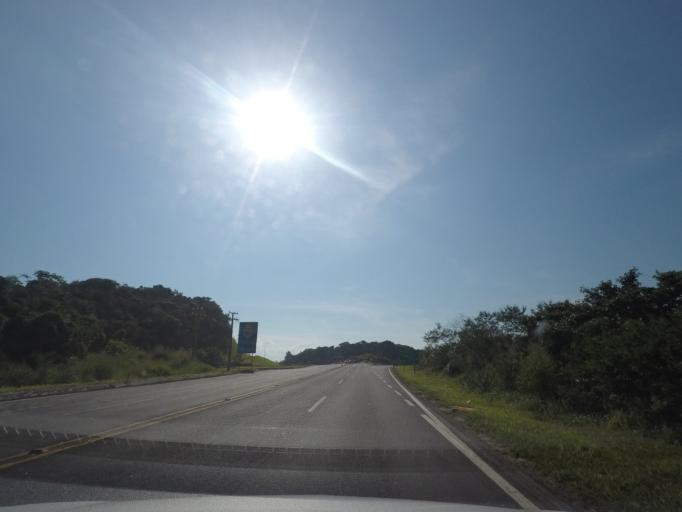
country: BR
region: Parana
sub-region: Paranagua
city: Paranagua
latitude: -25.5709
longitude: -48.6140
